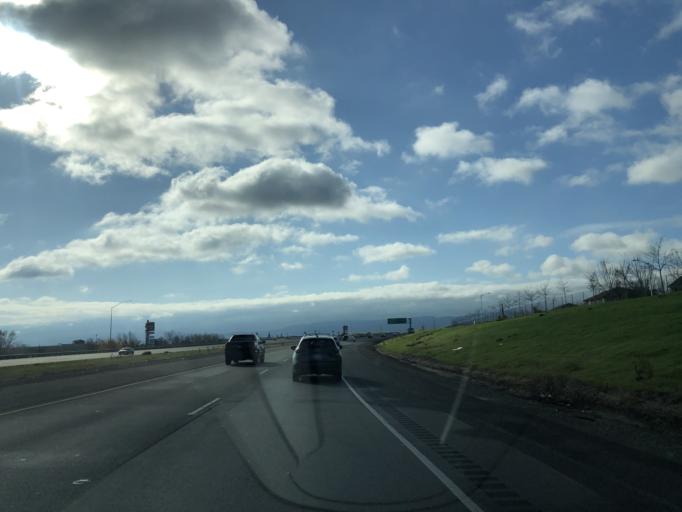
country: US
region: California
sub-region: Contra Costa County
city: Oakley
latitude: 37.9677
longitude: -121.7394
